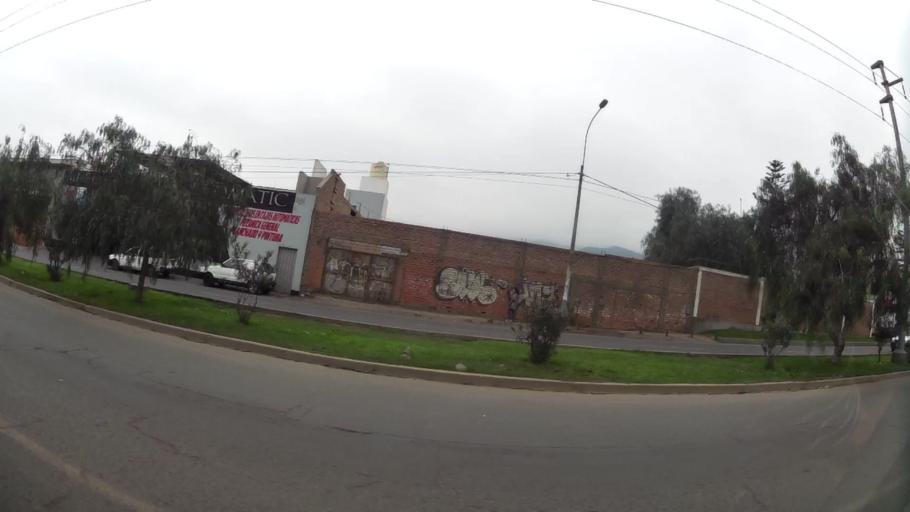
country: PE
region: Lima
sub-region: Lima
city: La Molina
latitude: -12.0861
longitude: -76.8965
